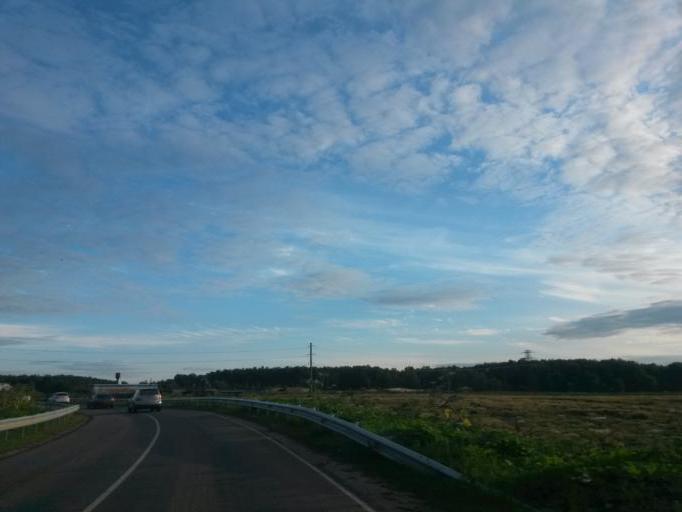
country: RU
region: Moskovskaya
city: Belyye Stolby
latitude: 55.2643
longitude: 37.7643
